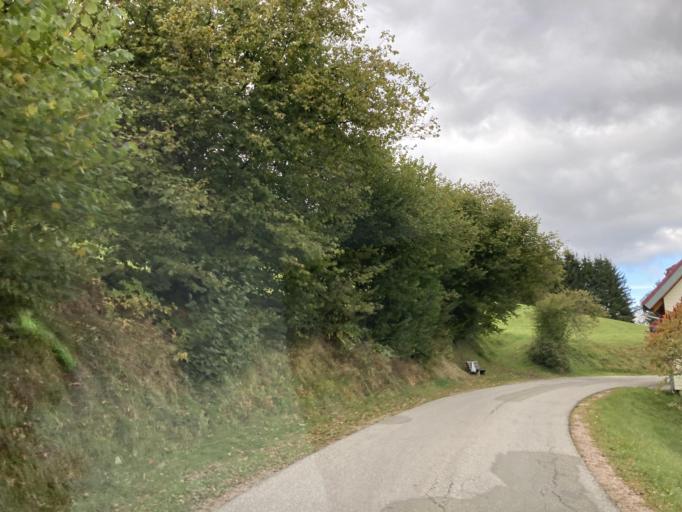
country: DE
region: Baden-Wuerttemberg
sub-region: Freiburg Region
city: Vohrenbach
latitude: 48.0493
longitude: 8.3021
